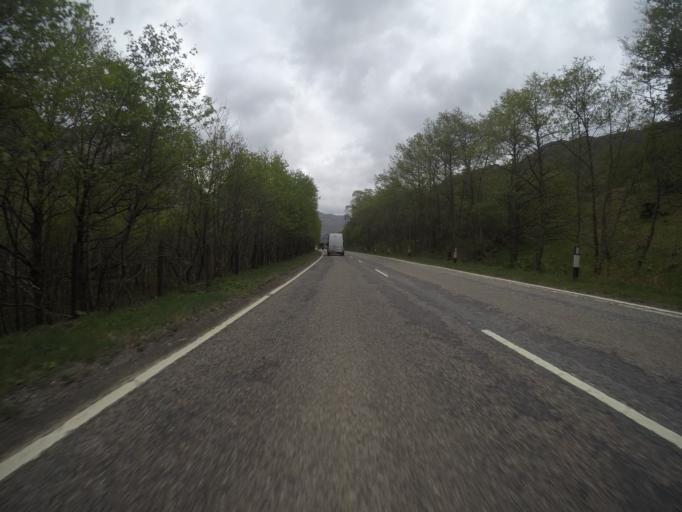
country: GB
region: Scotland
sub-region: Highland
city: Fort William
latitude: 57.1984
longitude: -5.3923
